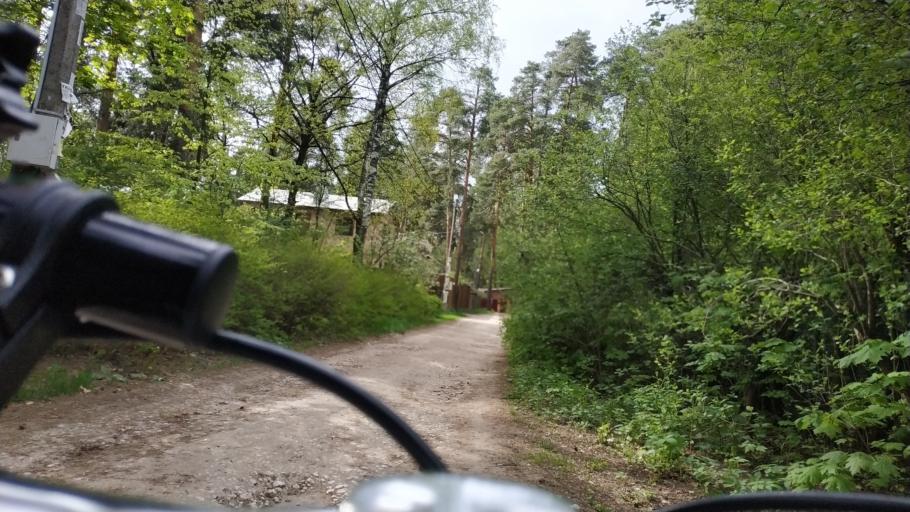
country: RU
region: Moskovskaya
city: Kratovo
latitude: 55.5782
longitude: 38.1829
